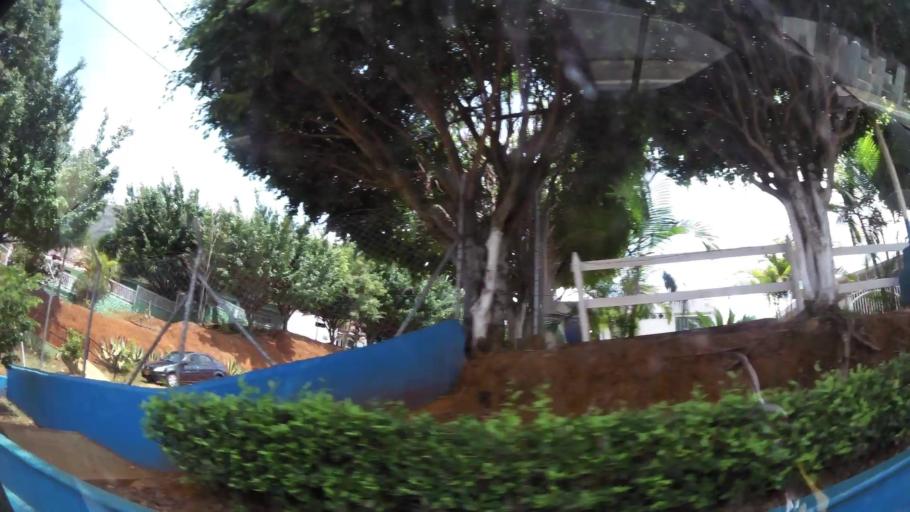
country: CO
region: Antioquia
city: Bello
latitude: 6.3450
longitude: -75.5451
